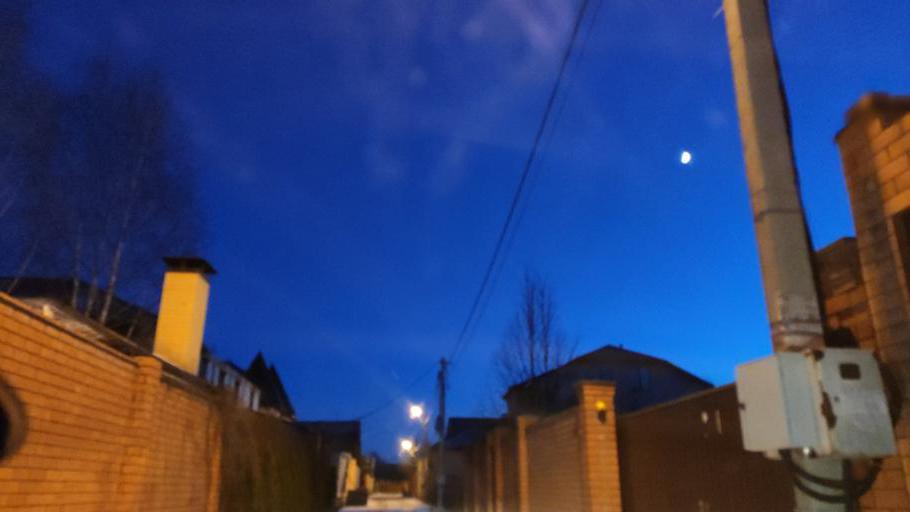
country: RU
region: Moskovskaya
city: Mosrentgen
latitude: 55.6324
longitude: 37.4517
